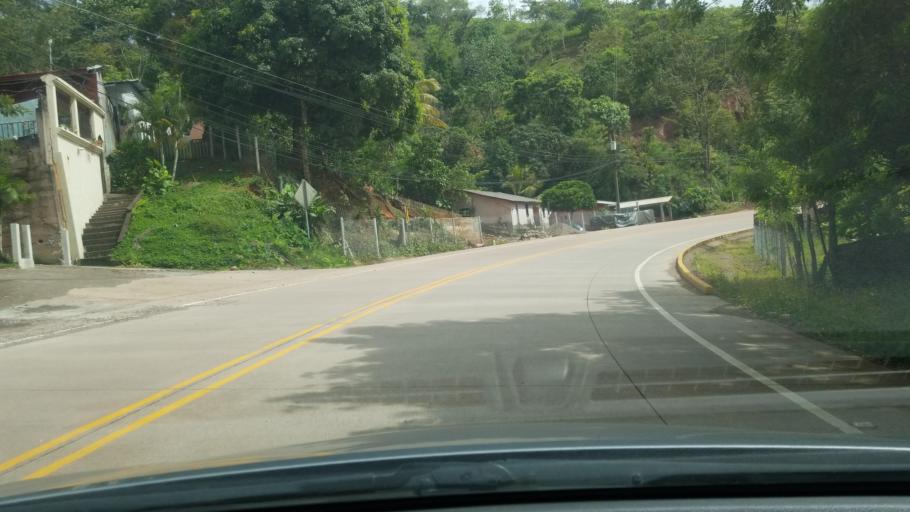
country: HN
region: Copan
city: Buenos Aires
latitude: 14.9257
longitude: -88.9752
